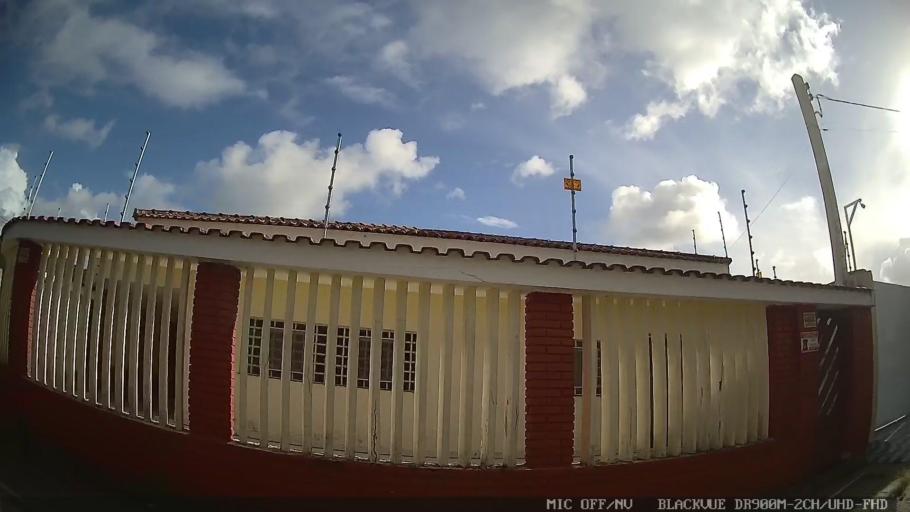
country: BR
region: Sao Paulo
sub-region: Itanhaem
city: Itanhaem
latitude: -24.1975
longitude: -46.8071
